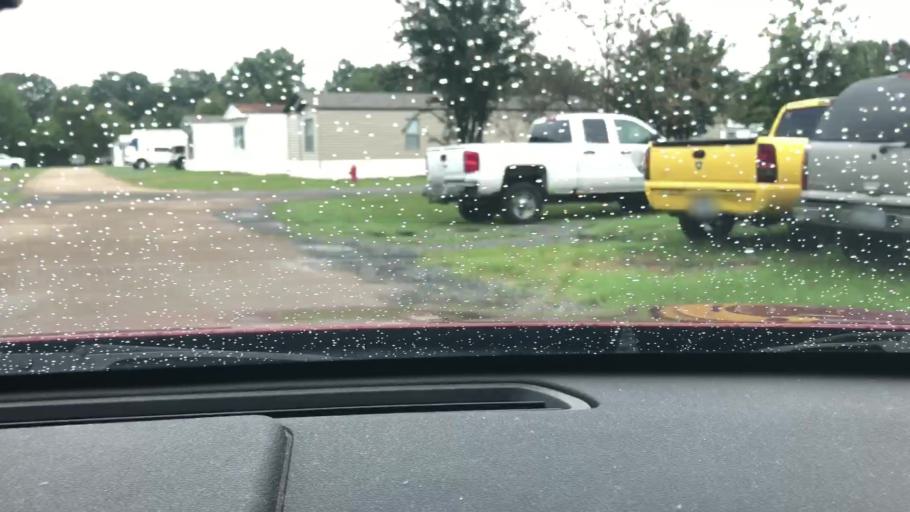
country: US
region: Texas
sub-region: Bowie County
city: Nash
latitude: 33.4439
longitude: -94.1383
